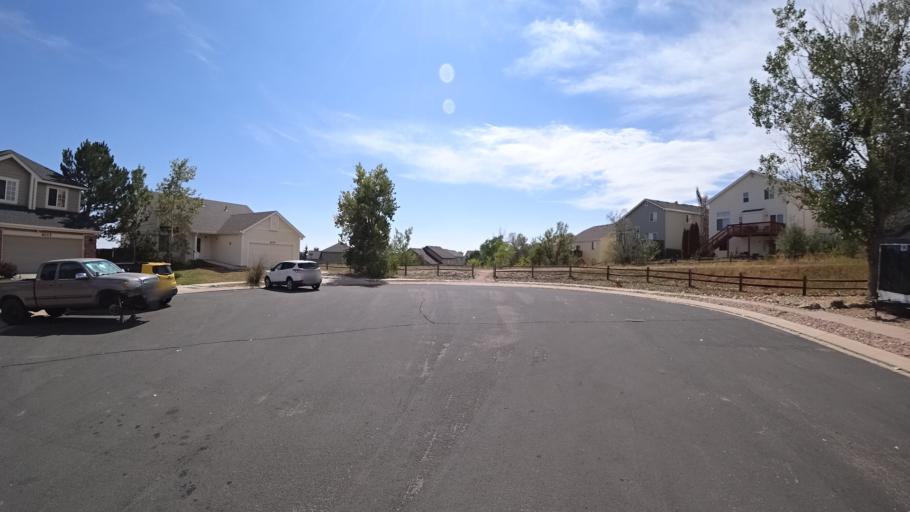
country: US
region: Colorado
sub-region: El Paso County
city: Cimarron Hills
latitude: 38.8992
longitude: -104.7168
